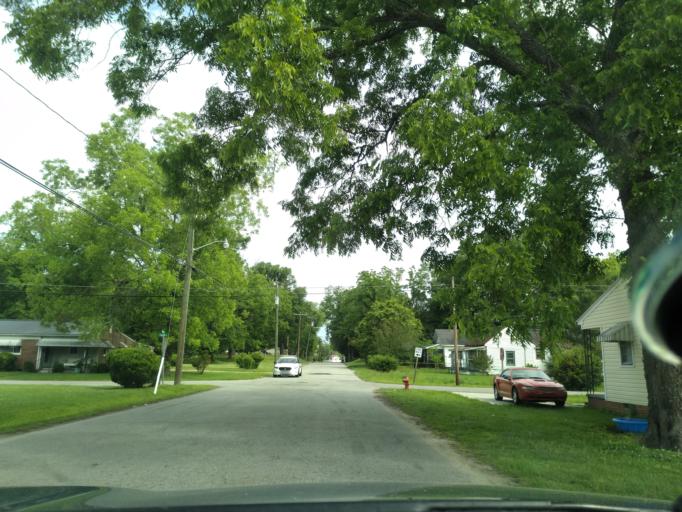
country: US
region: North Carolina
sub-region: Washington County
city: Plymouth
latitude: 35.8624
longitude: -76.7515
